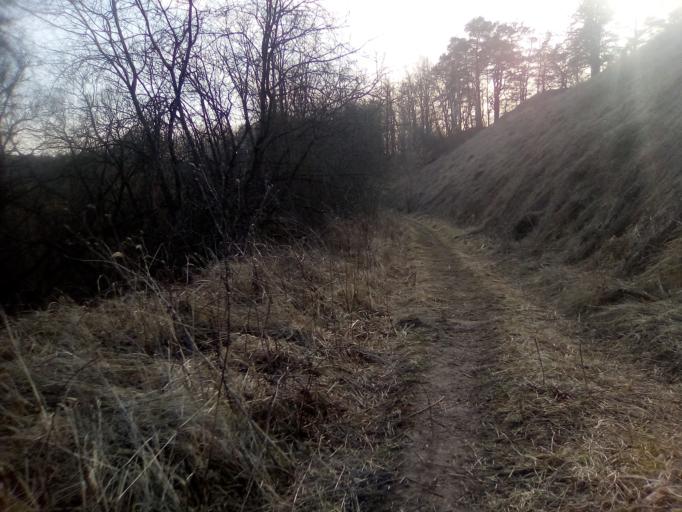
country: RU
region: Moskovskaya
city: Dubrovitsy
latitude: 55.4491
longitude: 37.4436
